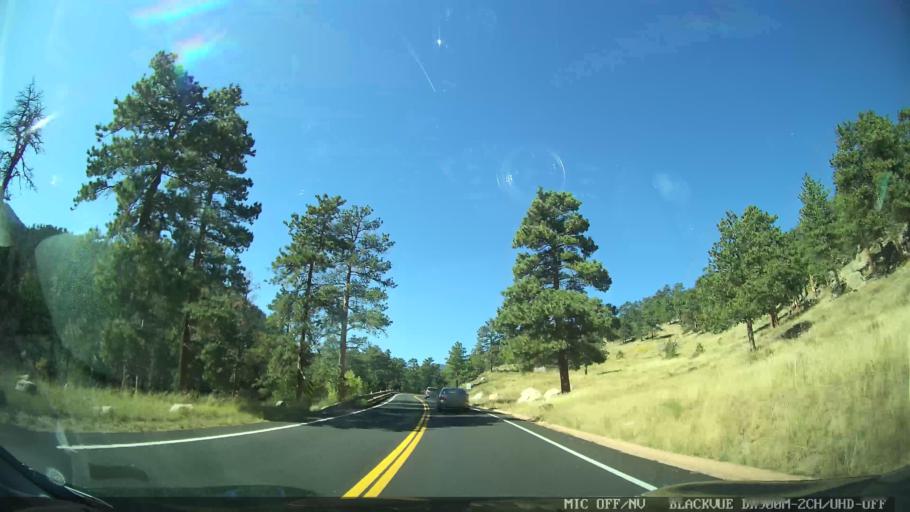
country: US
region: Colorado
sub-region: Larimer County
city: Estes Park
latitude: 40.3461
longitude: -105.5847
